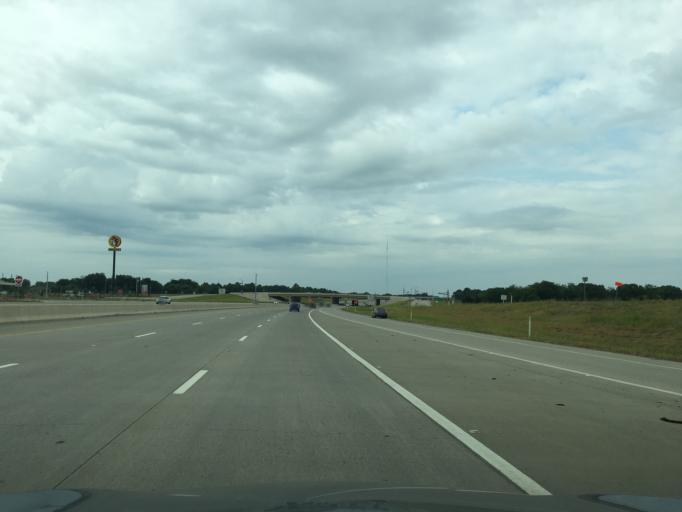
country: US
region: Texas
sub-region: Collin County
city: Melissa
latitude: 33.2738
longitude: -96.5934
